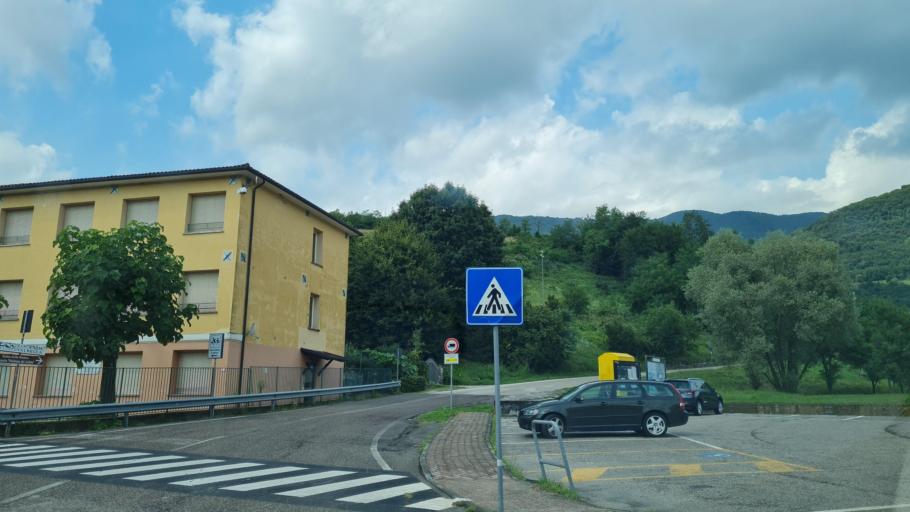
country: IT
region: Veneto
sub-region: Provincia di Vicenza
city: Marostica
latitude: 45.7685
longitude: 11.6587
